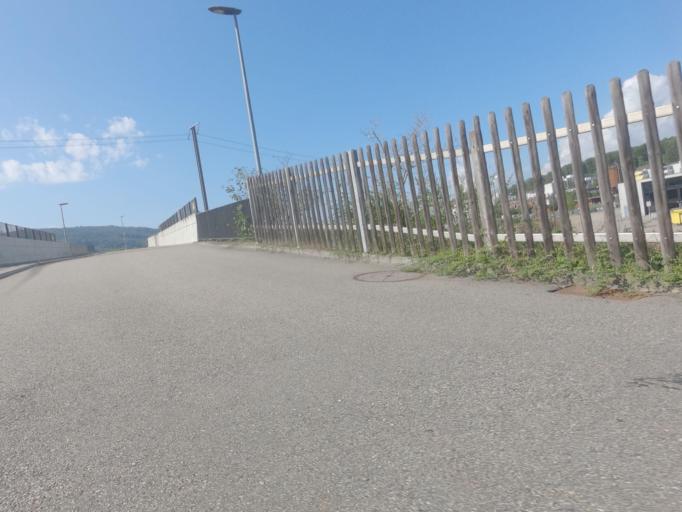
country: CH
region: Solothurn
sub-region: Bezirk Olten
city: Olten
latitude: 47.3493
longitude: 7.8951
